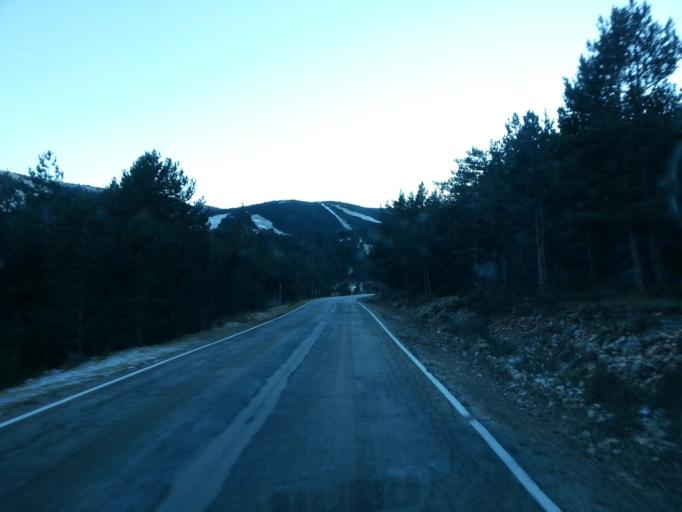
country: ES
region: Catalonia
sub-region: Provincia de Lleida
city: Gosol
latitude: 42.1816
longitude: 1.5585
